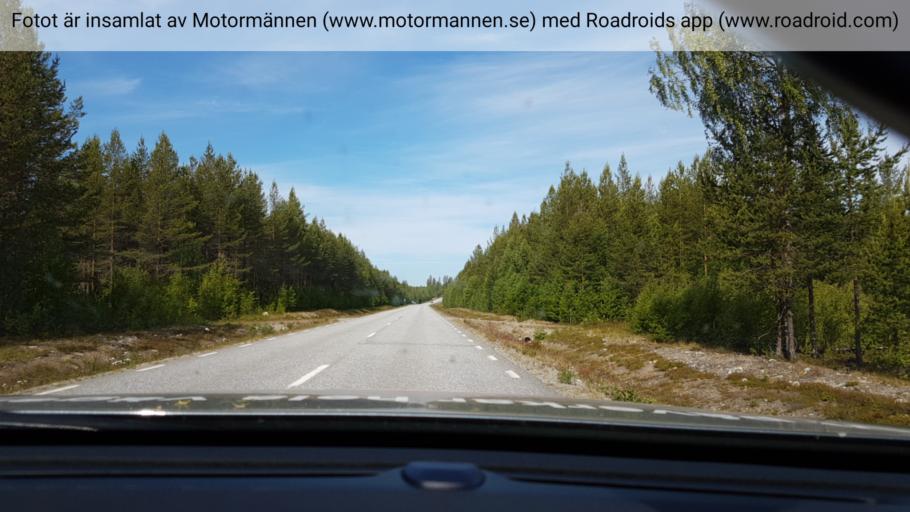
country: SE
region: Vaesterbotten
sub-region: Asele Kommun
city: Asele
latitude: 64.2200
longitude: 16.8810
